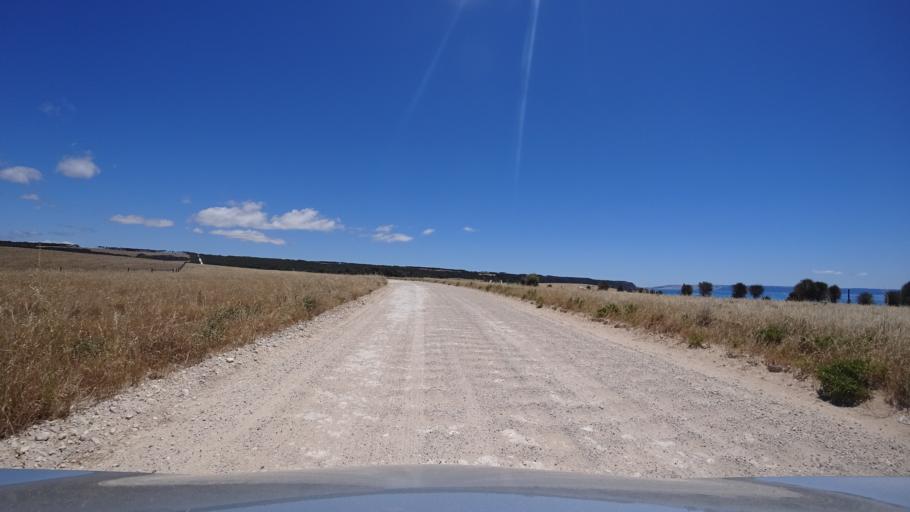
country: AU
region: South Australia
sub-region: Yankalilla
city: Normanville
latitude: -35.8416
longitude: 138.1267
